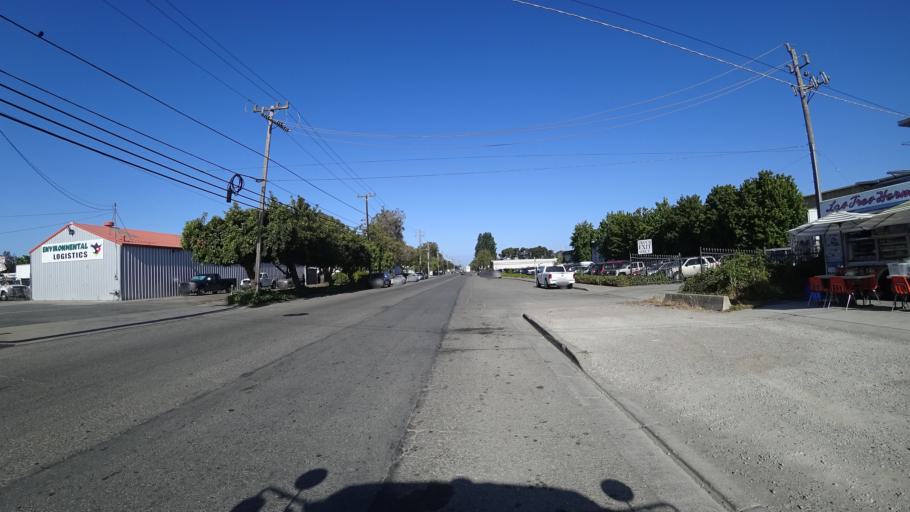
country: US
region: California
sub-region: Alameda County
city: San Lorenzo
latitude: 37.6385
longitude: -122.1232
